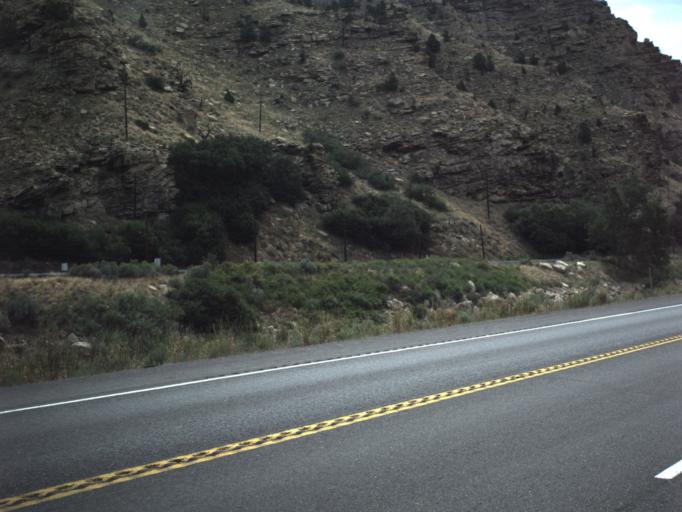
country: US
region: Utah
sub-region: Carbon County
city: Helper
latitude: 39.7566
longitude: -110.8892
